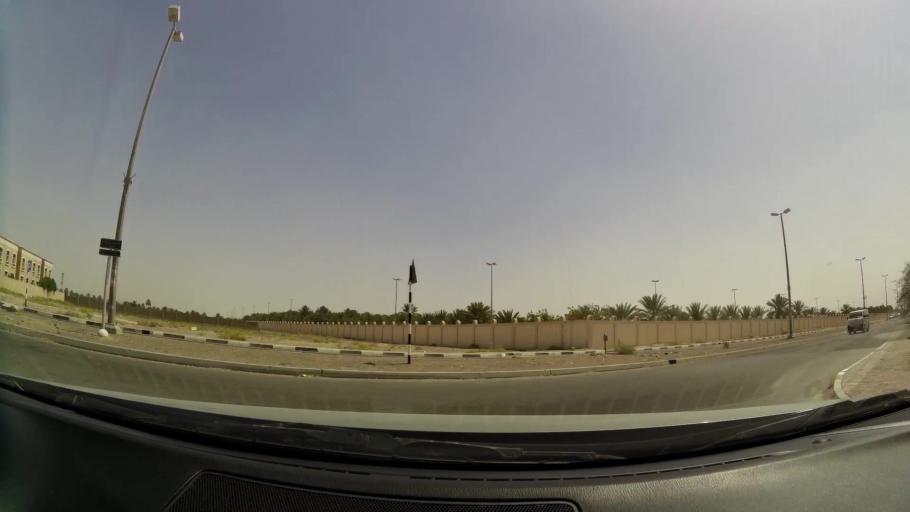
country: AE
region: Abu Dhabi
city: Al Ain
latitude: 24.2340
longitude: 55.7144
